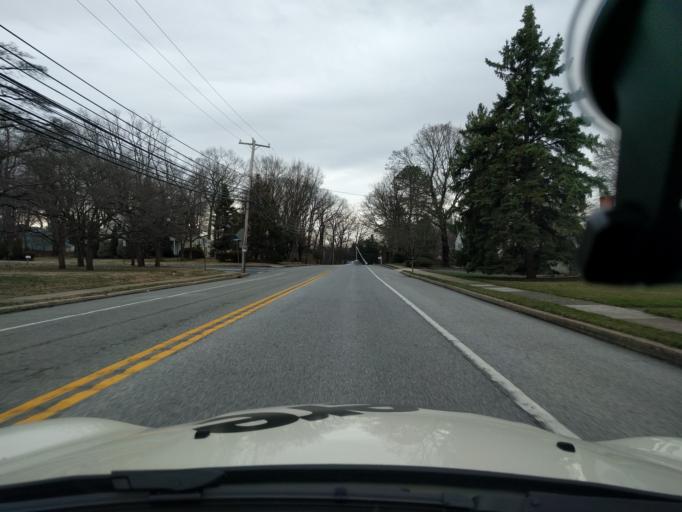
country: US
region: Pennsylvania
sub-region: Delaware County
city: Broomall
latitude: 39.9738
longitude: -75.3918
